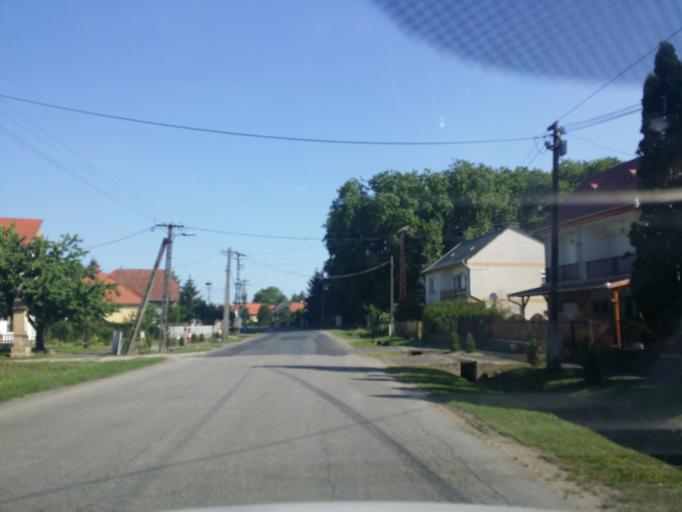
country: HU
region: Zala
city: Zalaszentgrot
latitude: 46.8716
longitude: 17.1148
